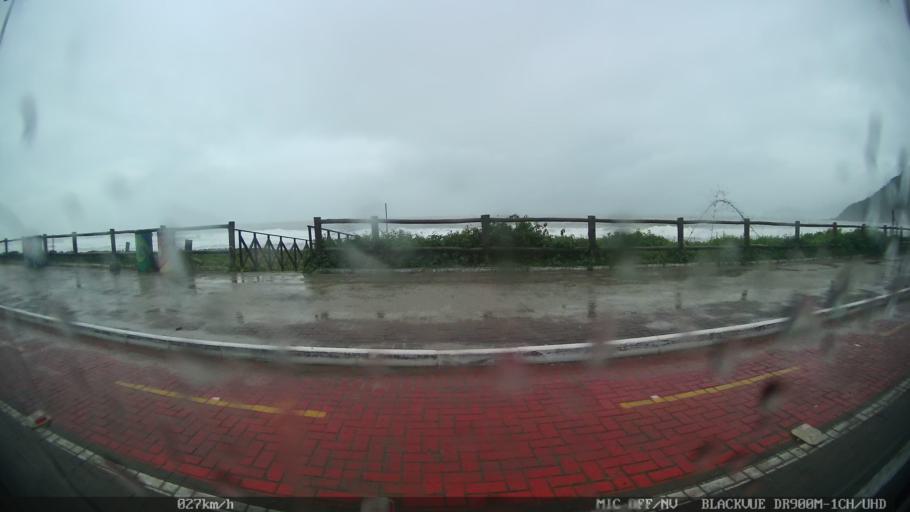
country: BR
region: Santa Catarina
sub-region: Balneario Camboriu
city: Balneario Camboriu
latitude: -26.9546
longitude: -48.6299
